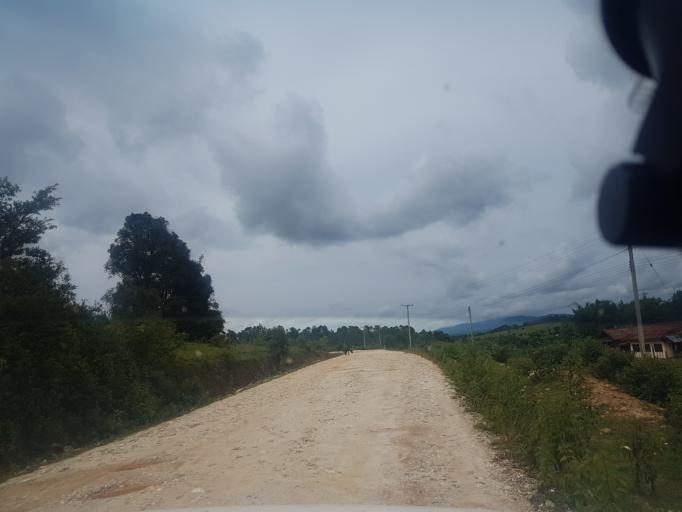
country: LA
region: Xiangkhoang
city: Phonsavan
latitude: 19.6039
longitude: 103.1069
